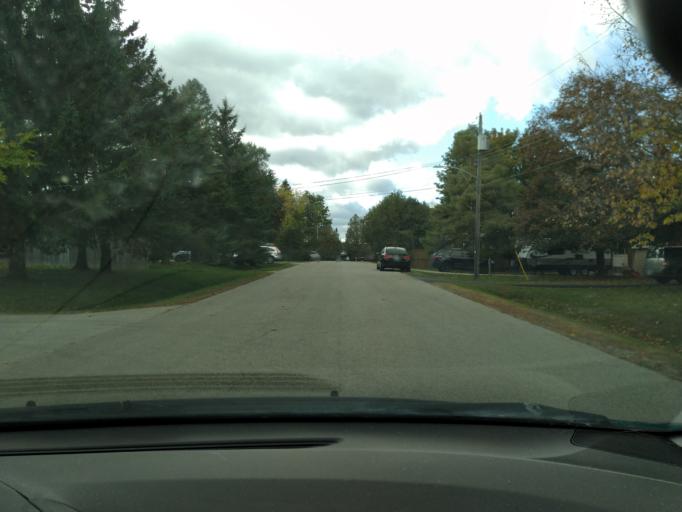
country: CA
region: Ontario
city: Bradford West Gwillimbury
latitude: 44.0864
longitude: -79.6783
